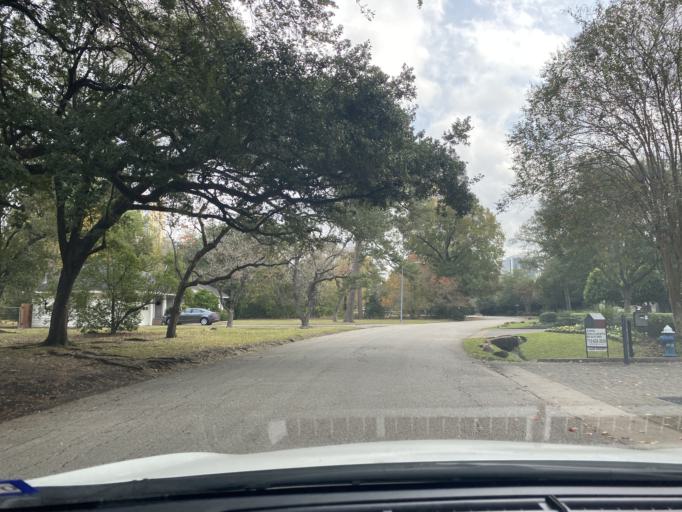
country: US
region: Texas
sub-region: Harris County
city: Hunters Creek Village
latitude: 29.7569
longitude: -95.4622
